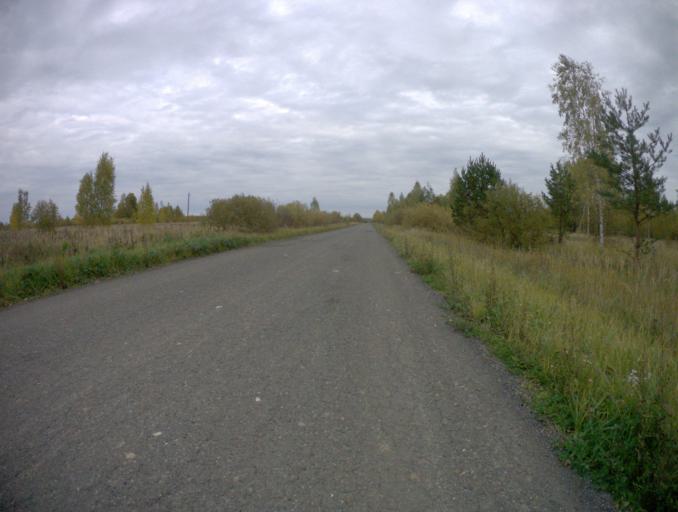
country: RU
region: Vladimir
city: Mstera
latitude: 56.3733
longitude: 41.8230
